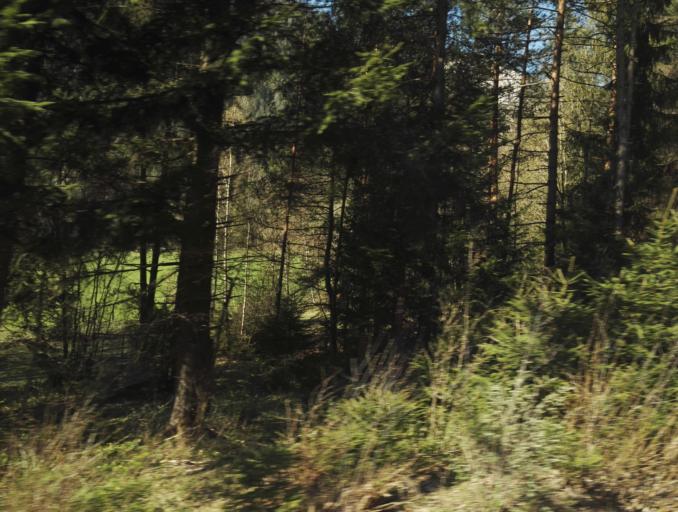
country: AT
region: Salzburg
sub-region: Politischer Bezirk Sankt Johann im Pongau
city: Forstau
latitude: 47.3983
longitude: 13.5900
